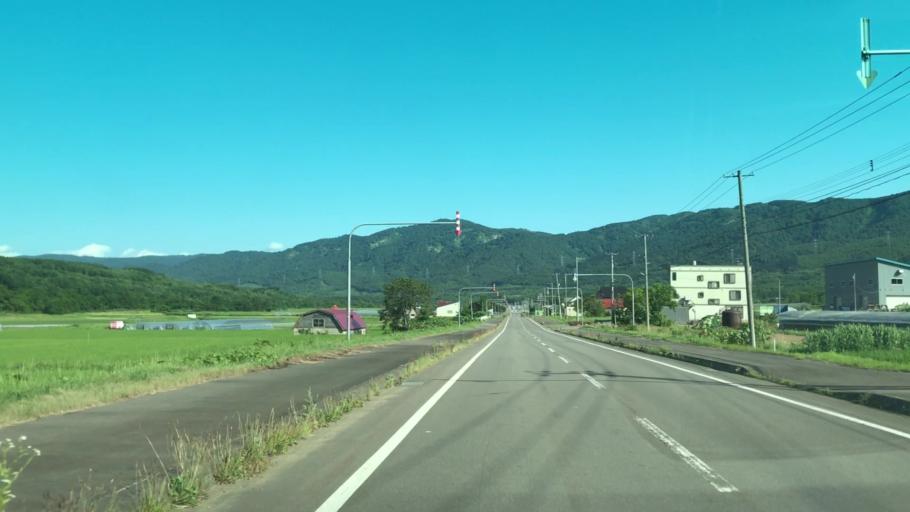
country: JP
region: Hokkaido
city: Yoichi
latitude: 43.0534
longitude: 140.7198
